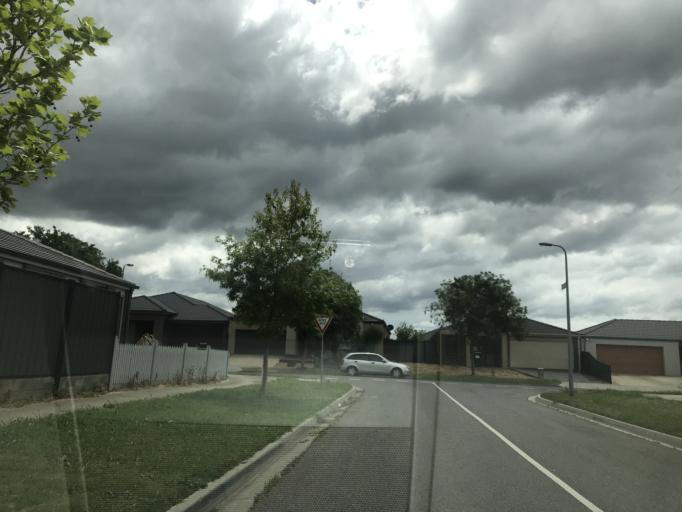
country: AU
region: Victoria
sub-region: Brimbank
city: Derrimut
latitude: -37.7855
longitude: 144.7558
